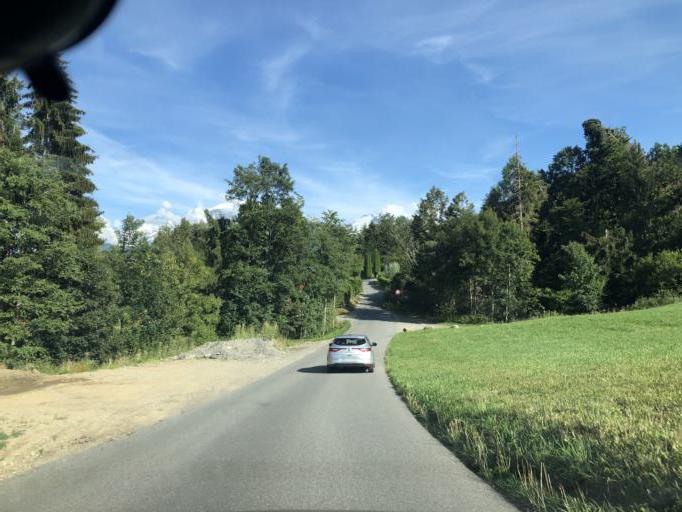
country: FR
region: Rhone-Alpes
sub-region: Departement de la Haute-Savoie
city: Cordon
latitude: 45.9134
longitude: 6.6185
